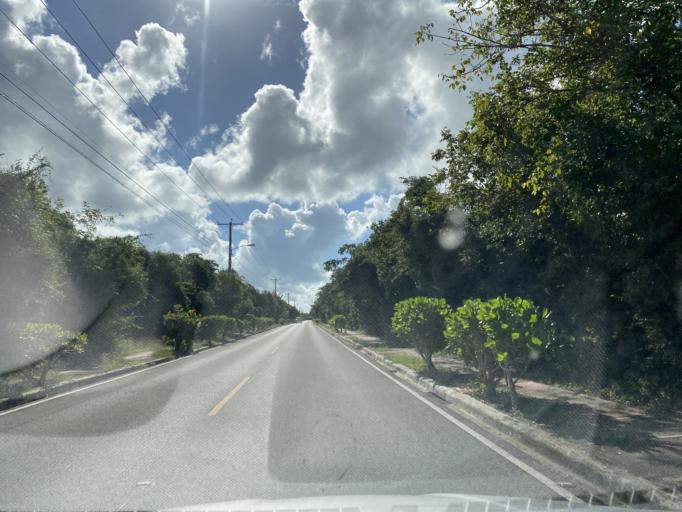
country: DO
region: La Altagracia
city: San Rafael del Yuma
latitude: 18.3381
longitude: -68.8109
